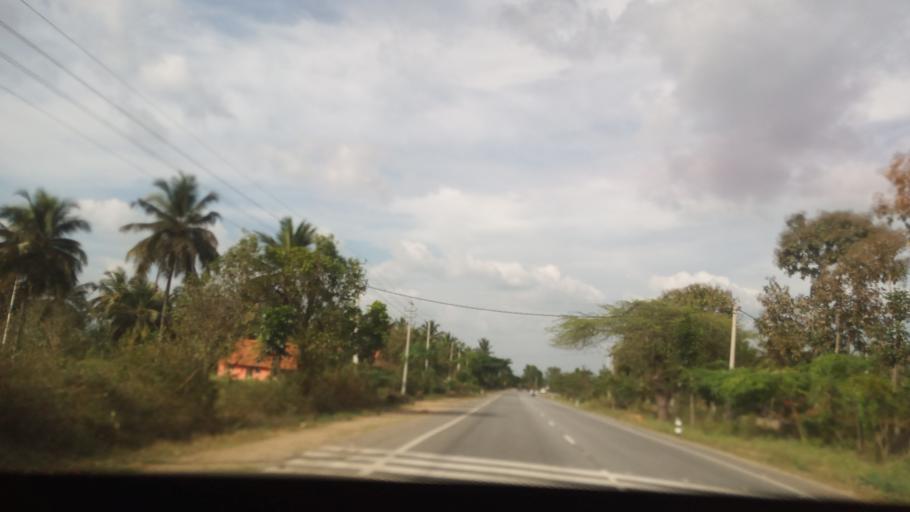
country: IN
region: Karnataka
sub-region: Mandya
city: Maddur
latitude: 12.6708
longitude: 77.0553
